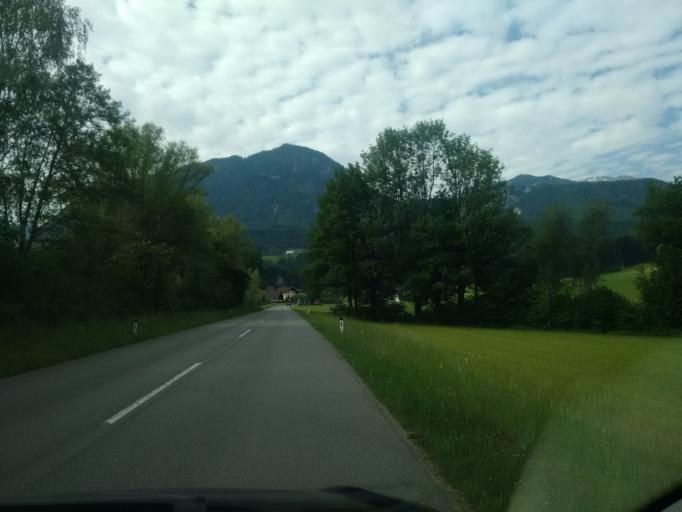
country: AT
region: Upper Austria
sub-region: Politischer Bezirk Kirchdorf an der Krems
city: Rossleithen
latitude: 47.7052
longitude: 14.3091
